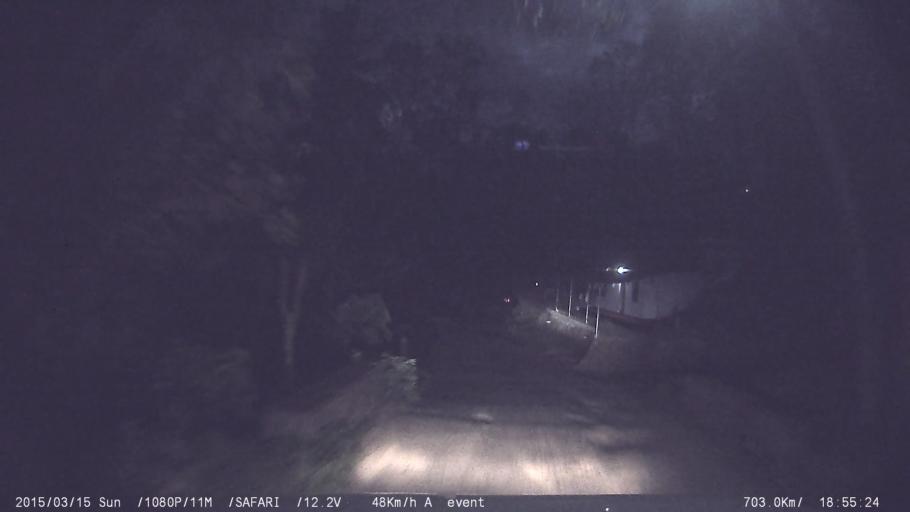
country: IN
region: Kerala
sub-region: Kottayam
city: Palackattumala
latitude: 9.8586
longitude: 76.6772
